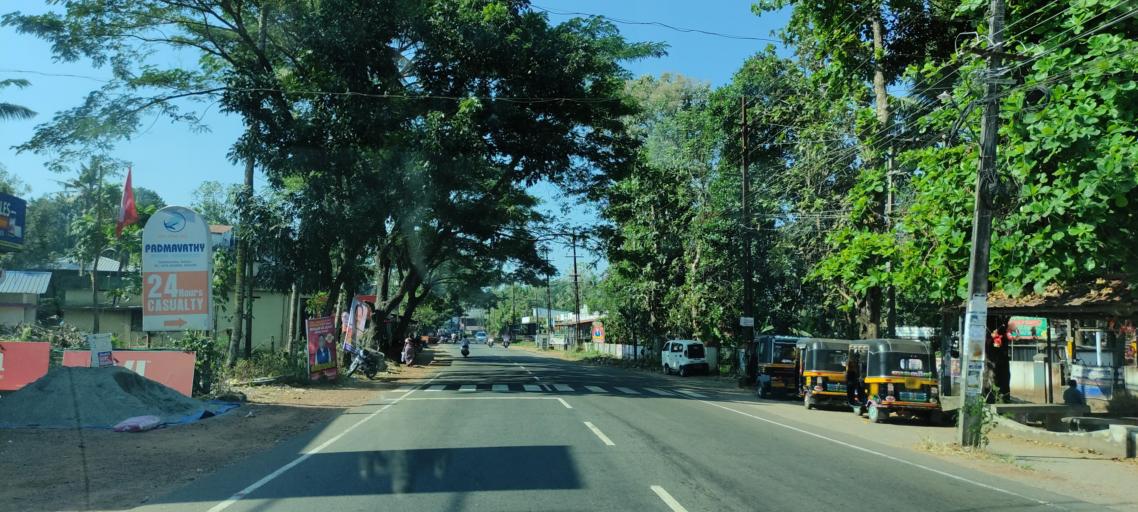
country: IN
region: Kerala
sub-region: Kollam
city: Panmana
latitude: 9.0528
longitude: 76.6338
